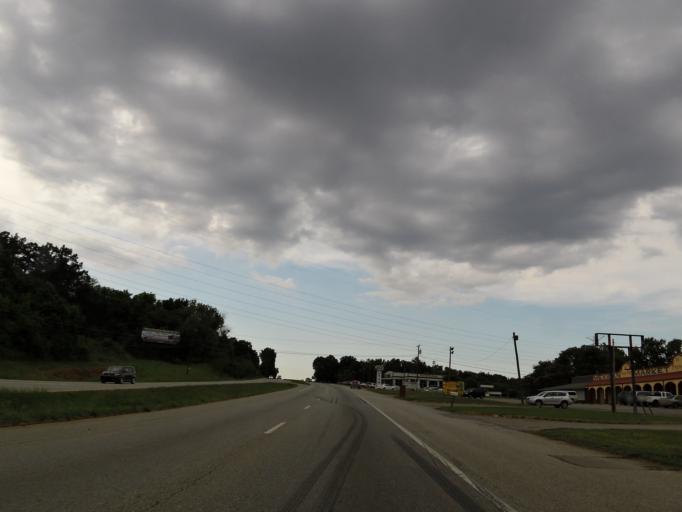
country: US
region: Tennessee
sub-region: Blount County
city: Eagleton Village
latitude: 35.8587
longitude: -83.9596
